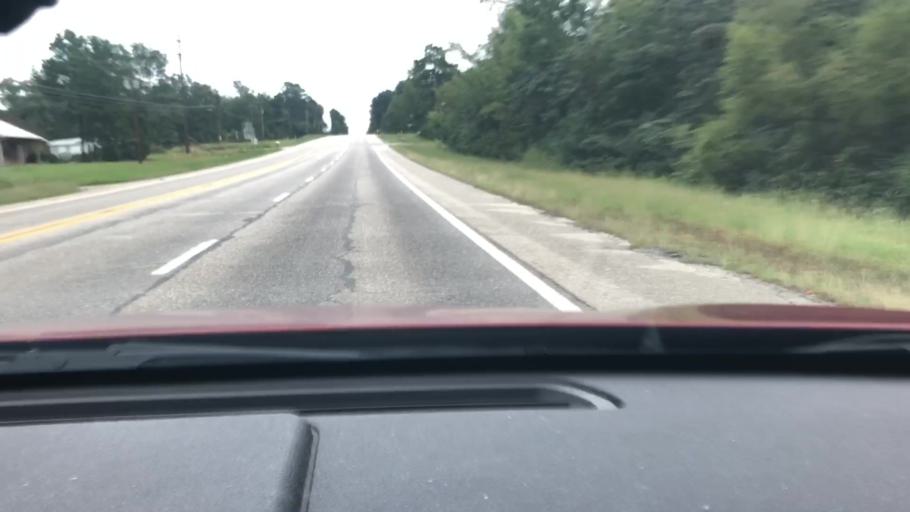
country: US
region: Arkansas
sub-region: Miller County
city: Texarkana
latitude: 33.4294
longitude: -93.9445
